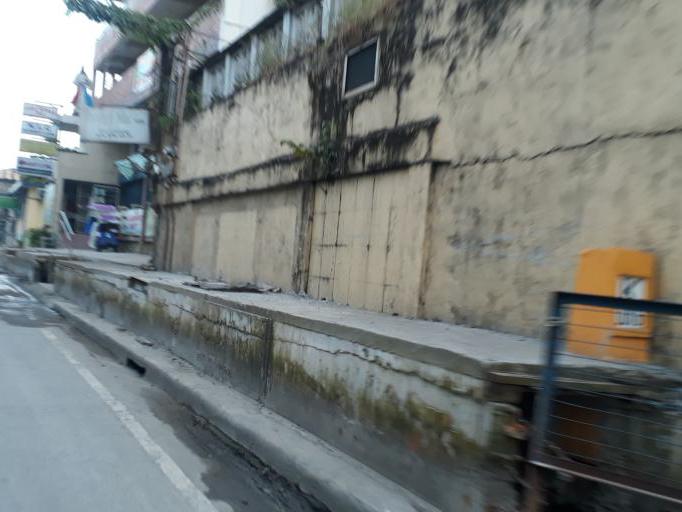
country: PH
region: Central Luzon
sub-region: Province of Bulacan
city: Obando
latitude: 14.7040
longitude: 120.9484
